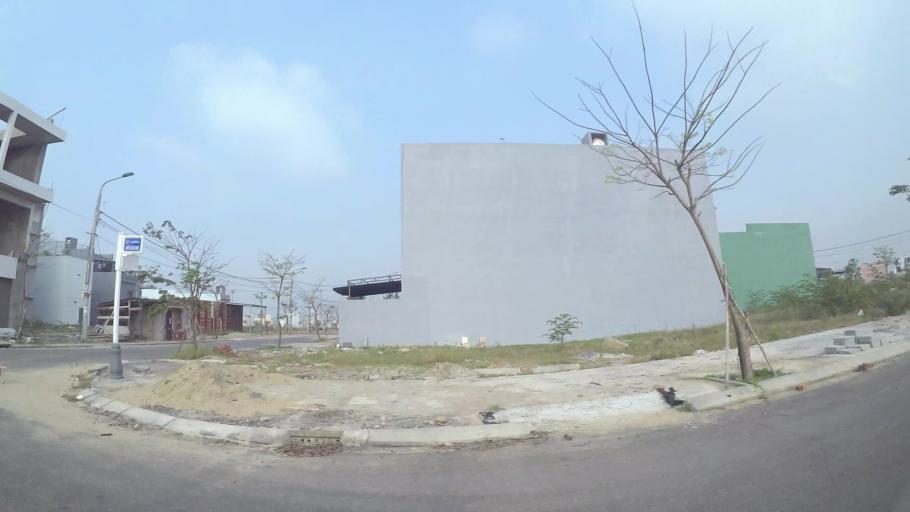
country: VN
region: Da Nang
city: Ngu Hanh Son
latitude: 16.0139
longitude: 108.2314
